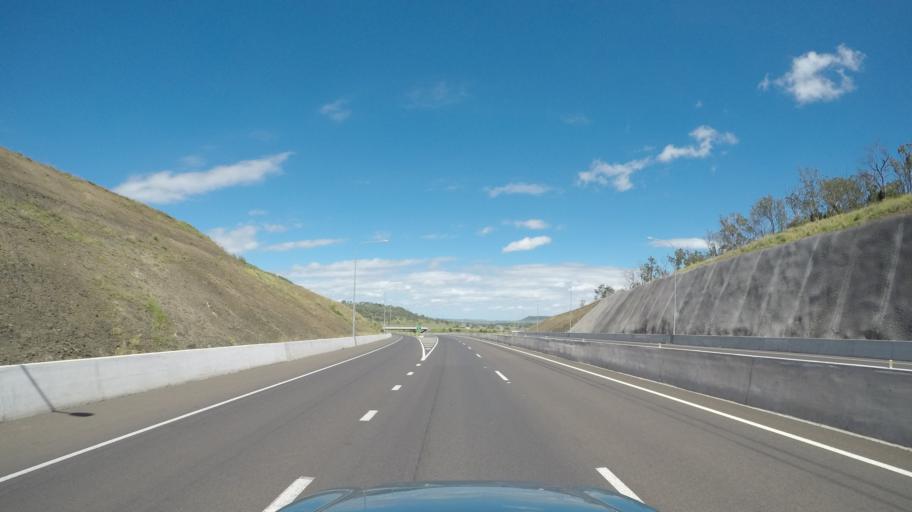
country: AU
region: Queensland
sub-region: Toowoomba
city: Wilsonton Heights
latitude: -27.5068
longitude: 151.9135
